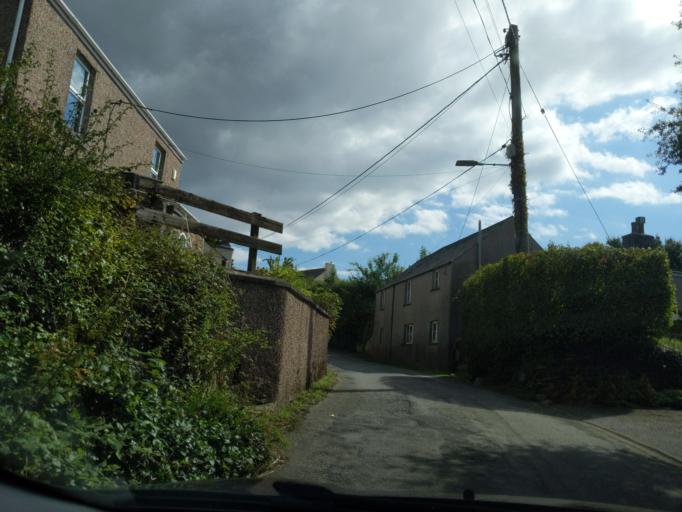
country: GB
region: England
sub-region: Plymouth
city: Plymstock
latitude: 50.3434
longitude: -4.0910
